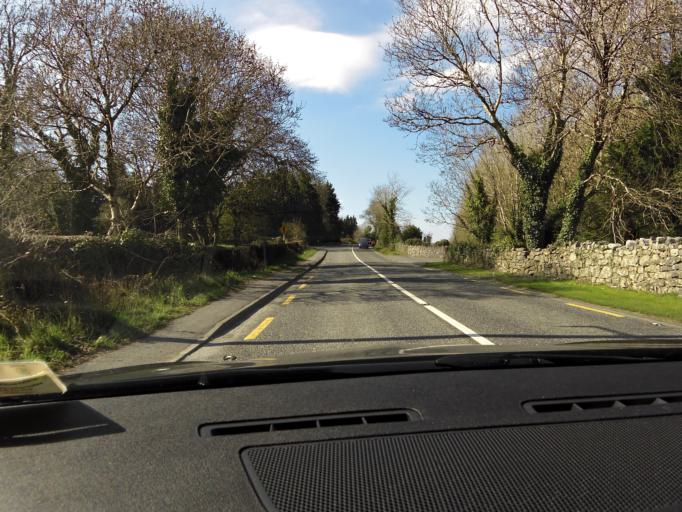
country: IE
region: Connaught
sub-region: County Galway
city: Gaillimh
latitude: 53.2998
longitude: -9.1013
